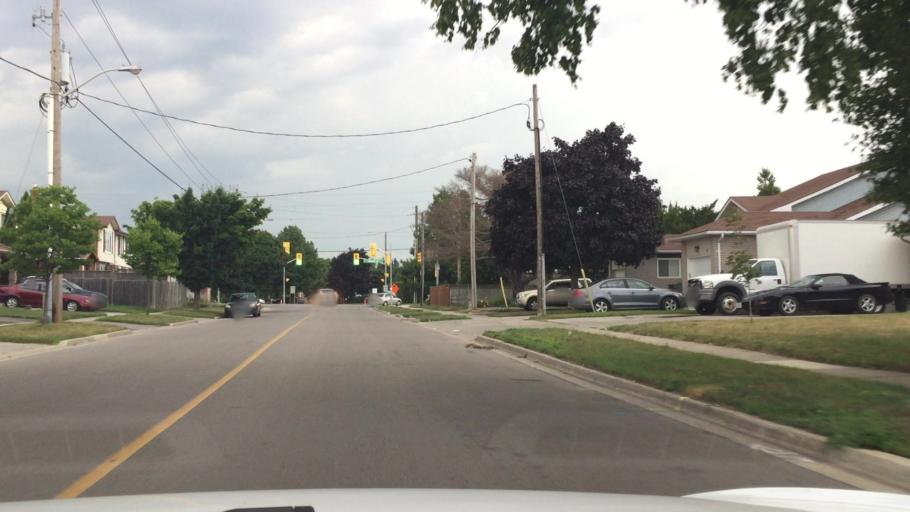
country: CA
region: Ontario
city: Oshawa
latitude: 43.9099
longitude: -78.8041
